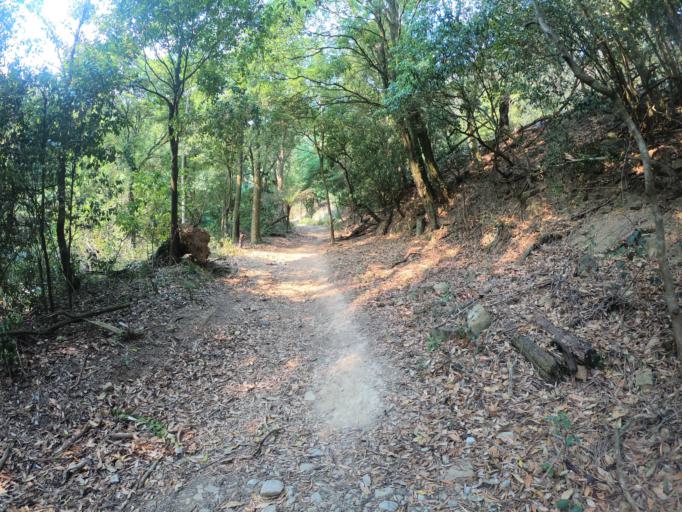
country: AU
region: New South Wales
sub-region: Wollongong
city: Mount Keira
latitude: -34.3989
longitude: 150.8512
